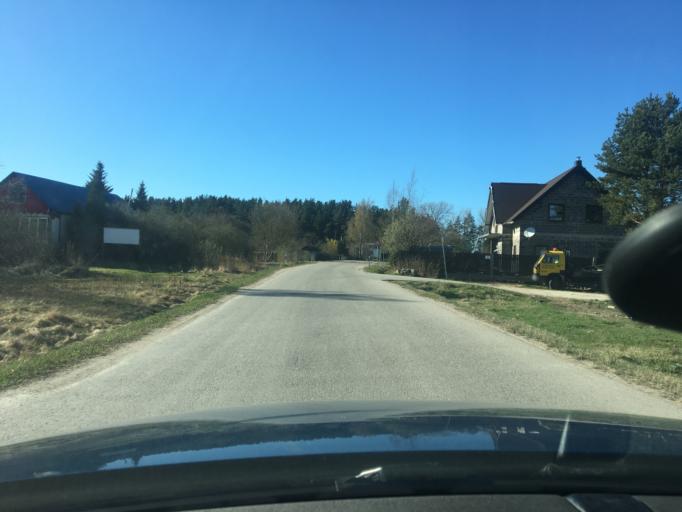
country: LV
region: Kekava
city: Kekava
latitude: 56.8533
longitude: 24.2578
